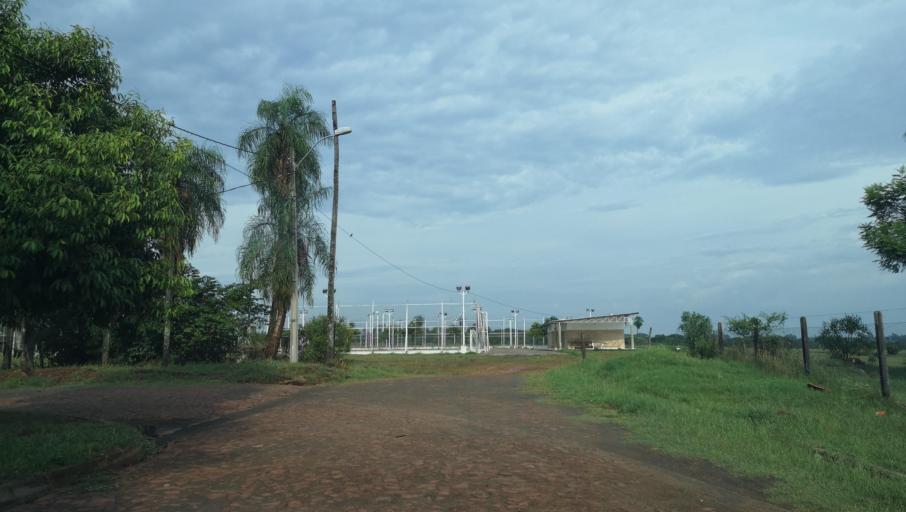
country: PY
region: Misiones
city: Santa Maria
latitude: -26.8784
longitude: -57.0340
